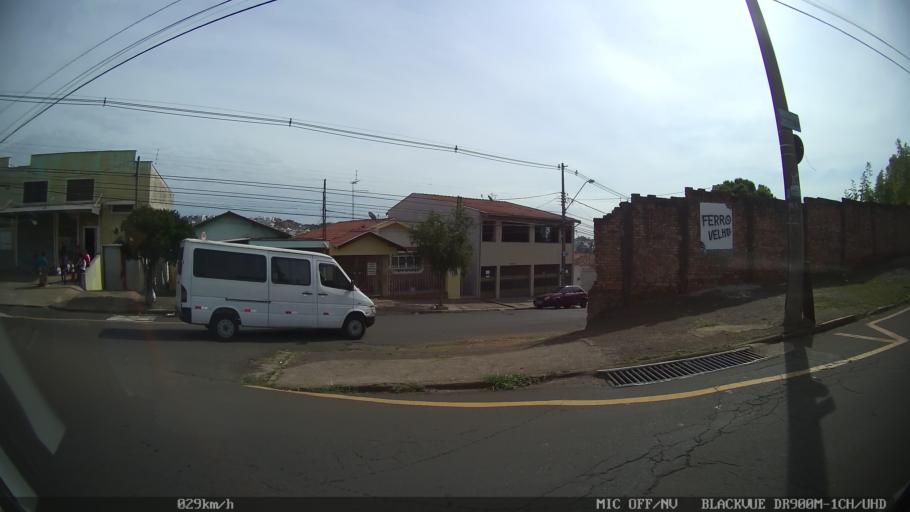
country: BR
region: Sao Paulo
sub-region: Piracicaba
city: Piracicaba
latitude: -22.7383
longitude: -47.6652
